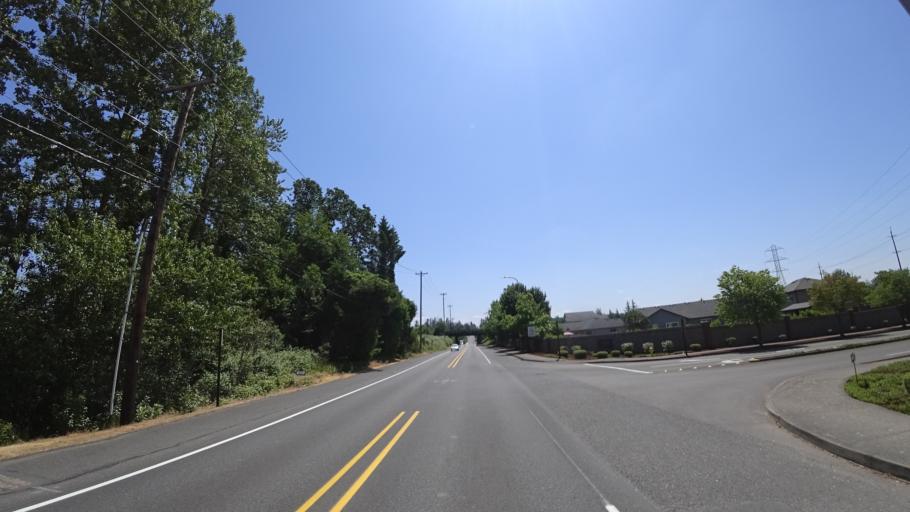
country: US
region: Oregon
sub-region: Multnomah County
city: Fairview
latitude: 45.5492
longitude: -122.4334
